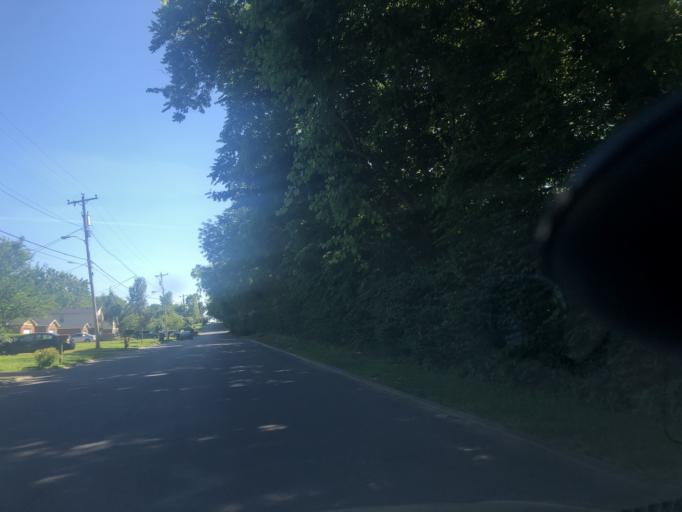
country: US
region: Tennessee
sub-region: Davidson County
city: Lakewood
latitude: 36.2418
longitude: -86.6705
